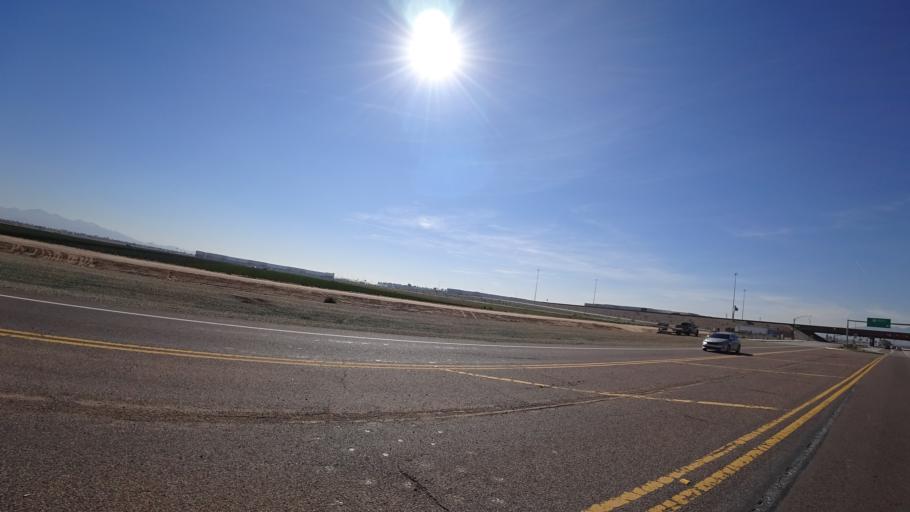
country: US
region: Arizona
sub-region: Maricopa County
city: Citrus Park
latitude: 33.5082
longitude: -112.4155
